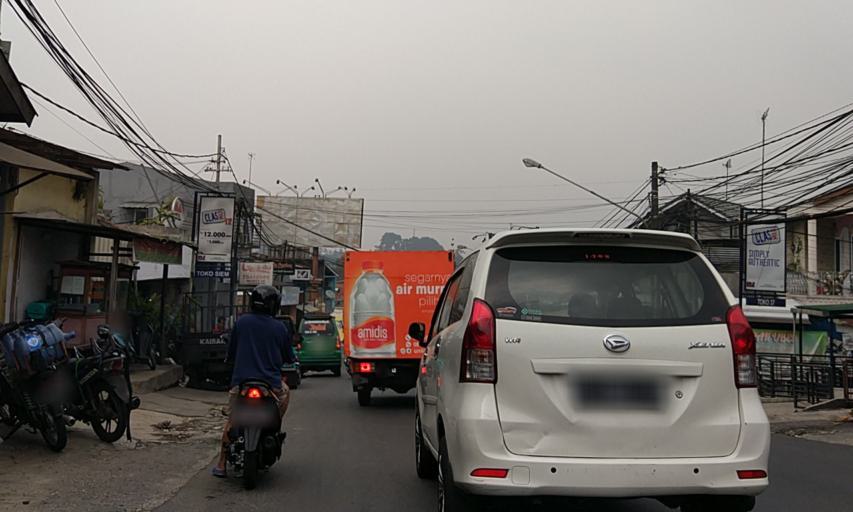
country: ID
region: West Java
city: Bandung
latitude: -6.8824
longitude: 107.6045
